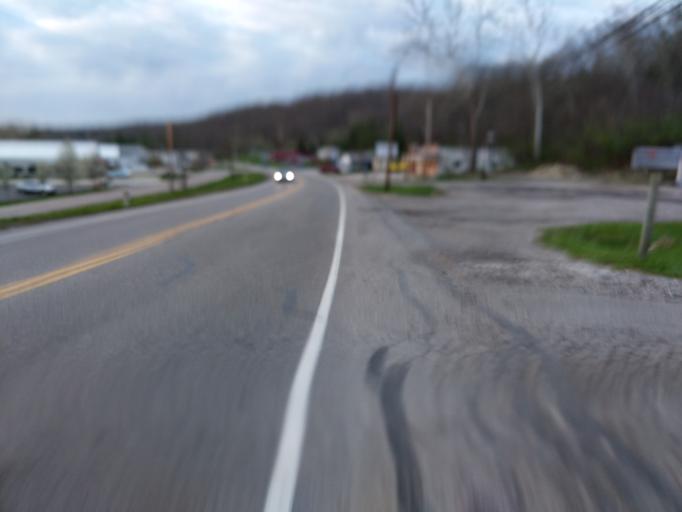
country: US
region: Ohio
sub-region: Athens County
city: Athens
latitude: 39.3466
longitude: -82.0954
